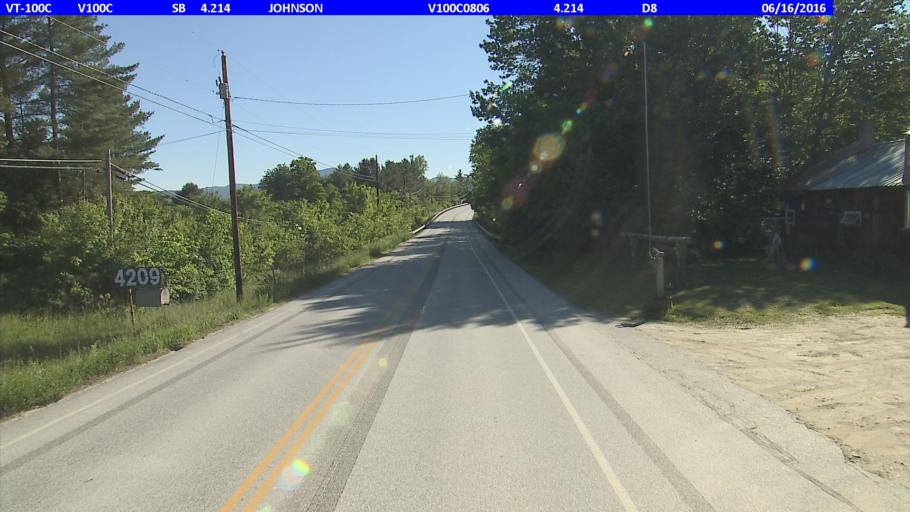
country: US
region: Vermont
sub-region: Lamoille County
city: Hyde Park
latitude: 44.6644
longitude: -72.6116
